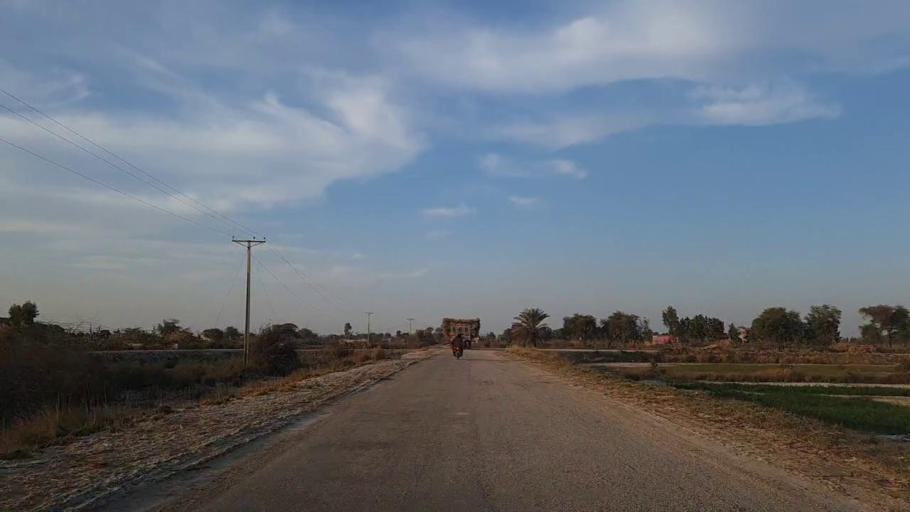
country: PK
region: Sindh
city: Bandhi
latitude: 26.5964
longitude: 68.3413
